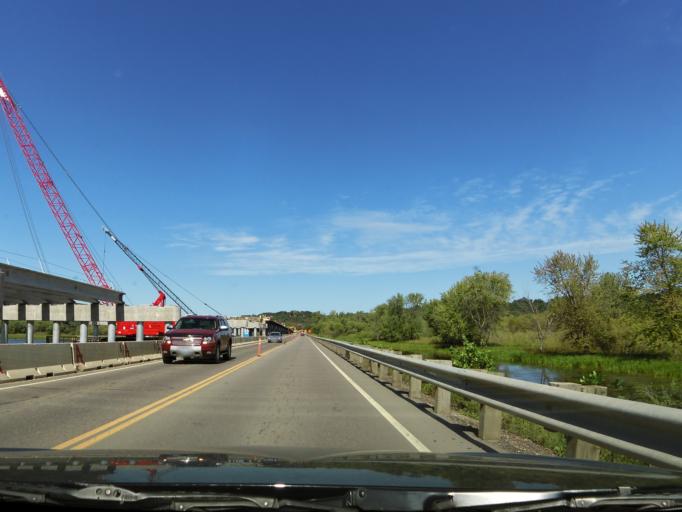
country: US
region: Minnesota
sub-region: Scott County
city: Shakopee
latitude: 44.8045
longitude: -93.5303
